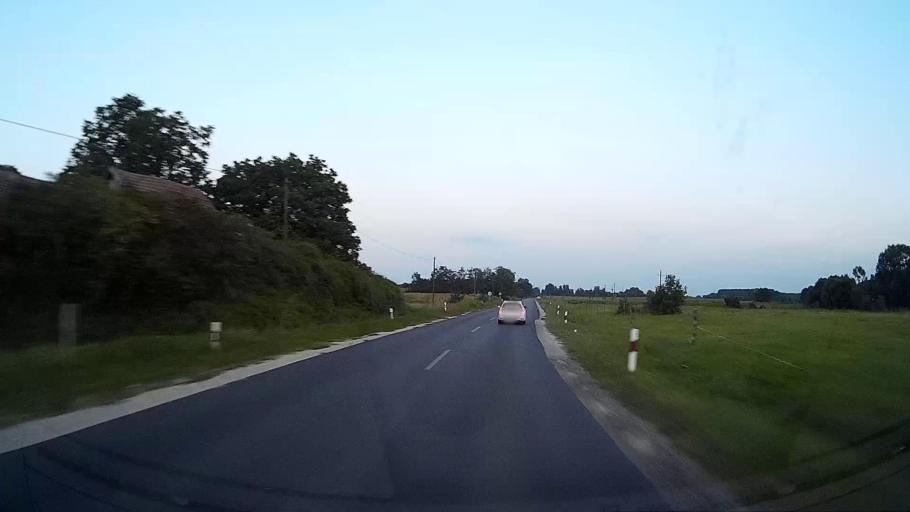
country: HU
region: Pest
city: Albertirsa
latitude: 47.2452
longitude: 19.6308
